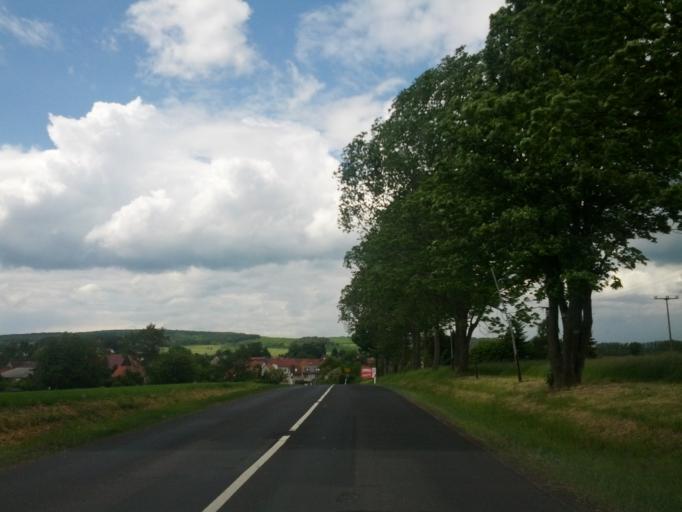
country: DE
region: Thuringia
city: Friedrichswerth
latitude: 51.0191
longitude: 10.5314
